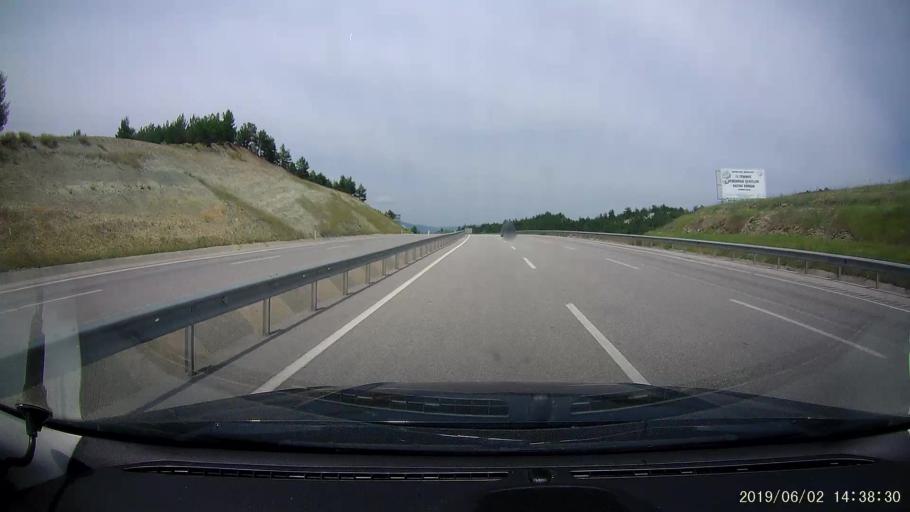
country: TR
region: Corum
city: Hacihamza
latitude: 41.0561
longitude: 34.2823
